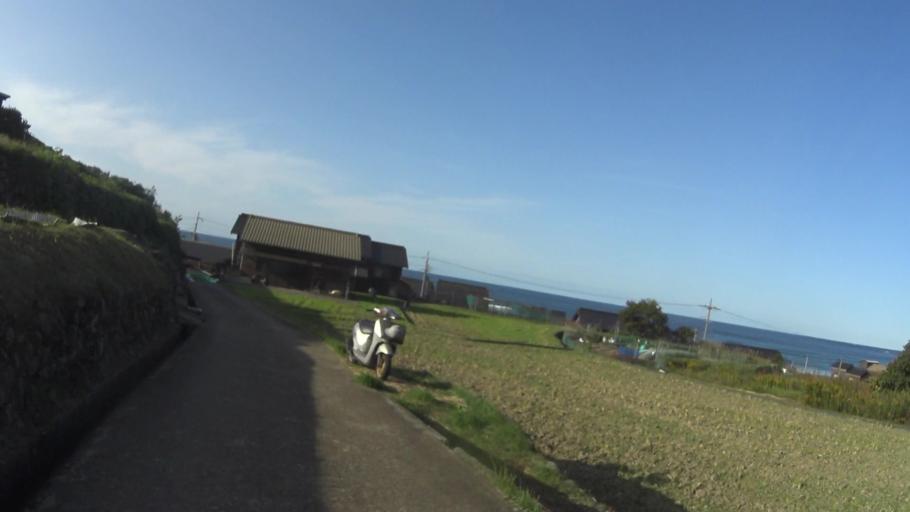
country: JP
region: Kyoto
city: Miyazu
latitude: 35.7624
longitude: 135.2065
